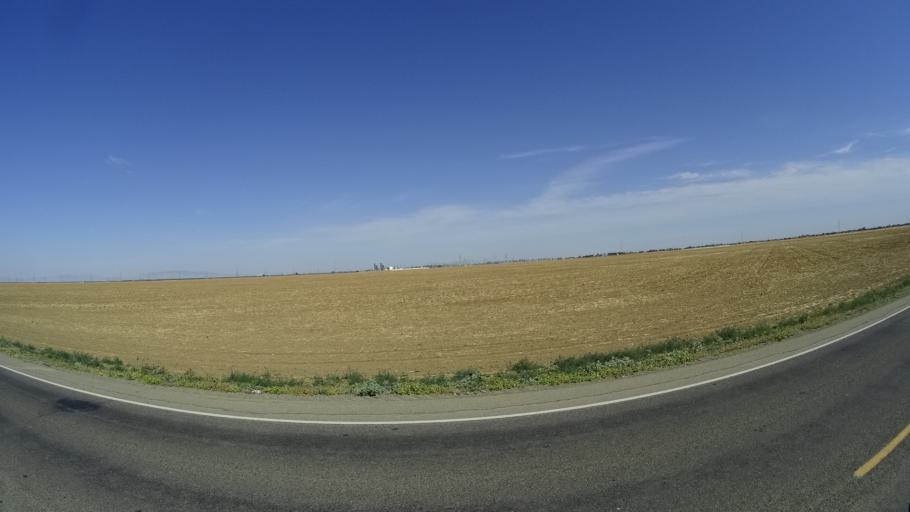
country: US
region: California
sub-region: Kings County
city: Lemoore Station
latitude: 36.2316
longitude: -119.8913
